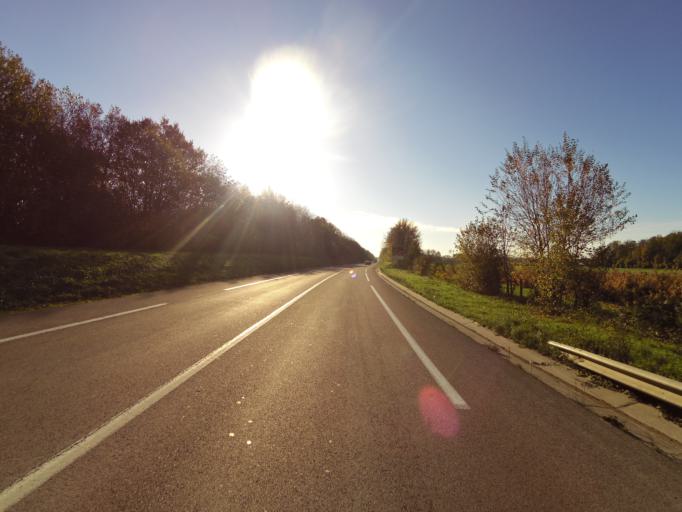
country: FR
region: Champagne-Ardenne
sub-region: Departement de l'Aube
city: Bucheres
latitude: 48.2469
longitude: 4.1161
